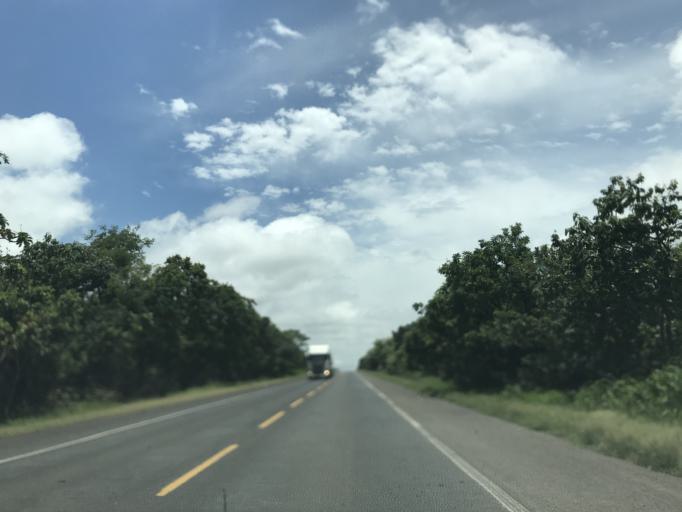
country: BR
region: Minas Gerais
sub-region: Prata
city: Prata
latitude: -19.6281
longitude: -48.9395
